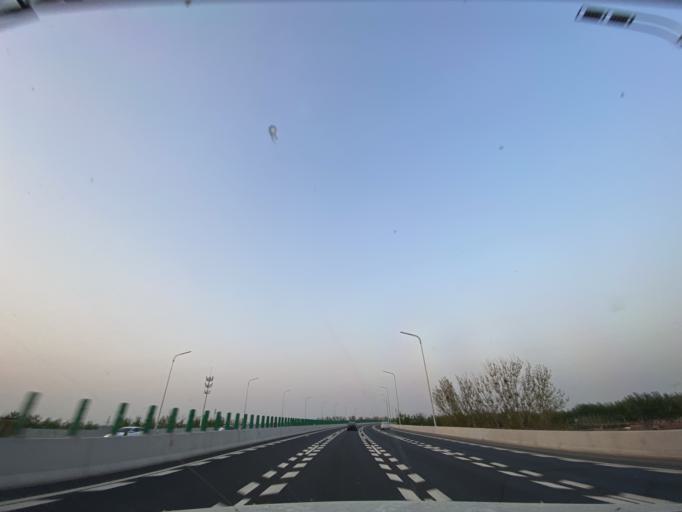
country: CN
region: Beijing
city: Xingfeng
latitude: 39.6884
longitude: 116.3652
